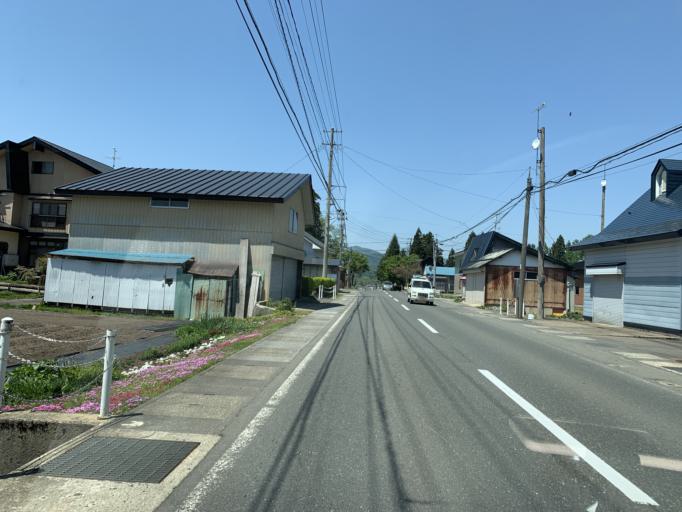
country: JP
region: Akita
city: Yokotemachi
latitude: 39.3988
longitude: 140.7565
